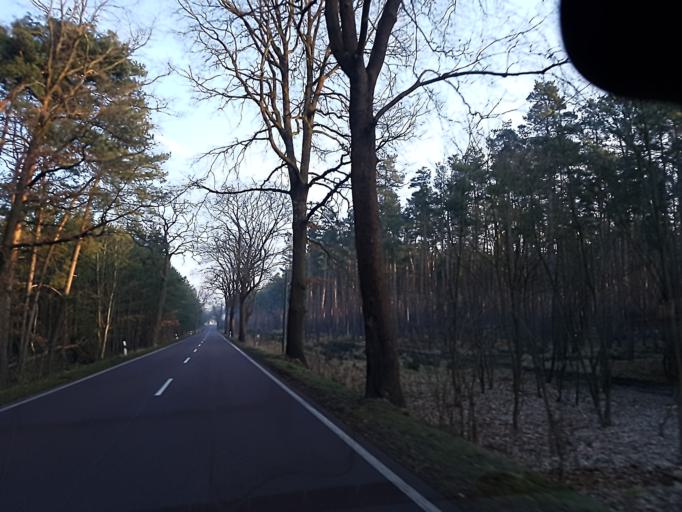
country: DE
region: Saxony-Anhalt
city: Coswig
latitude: 51.9841
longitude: 12.4690
